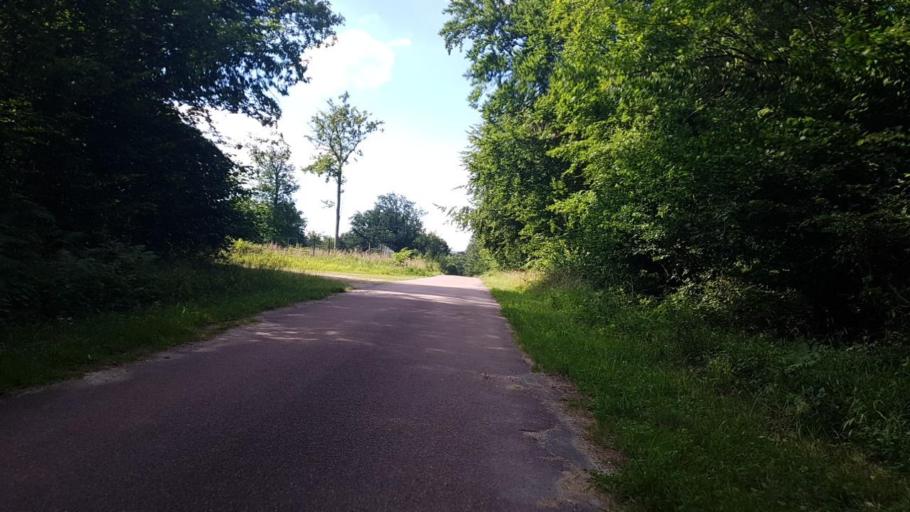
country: FR
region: Picardie
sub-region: Departement de l'Oise
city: Chamant
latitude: 49.1665
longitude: 2.6334
